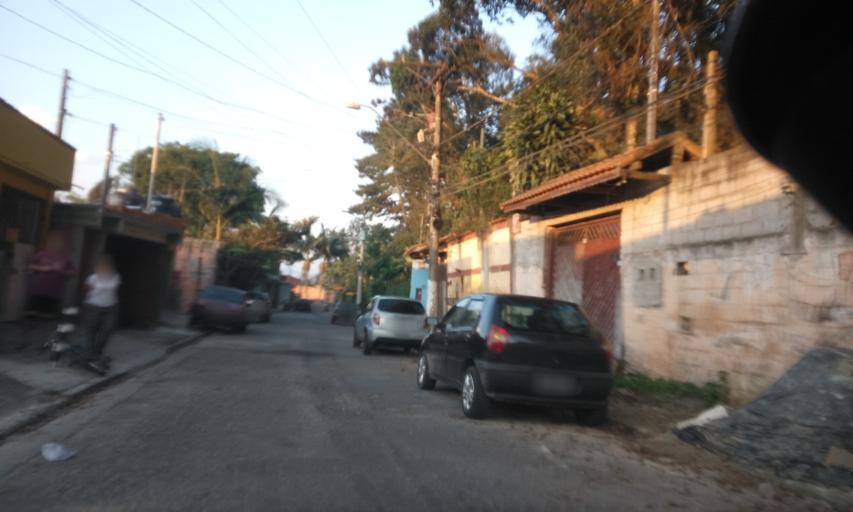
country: BR
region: Sao Paulo
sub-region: Sao Bernardo Do Campo
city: Sao Bernardo do Campo
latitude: -23.7945
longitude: -46.5448
